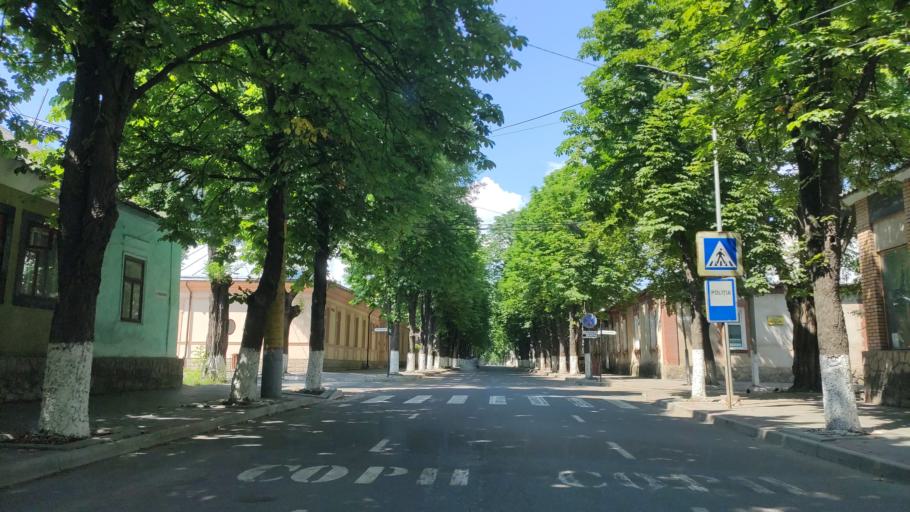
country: MD
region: Raionul Soroca
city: Soroca
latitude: 48.1525
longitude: 28.3021
